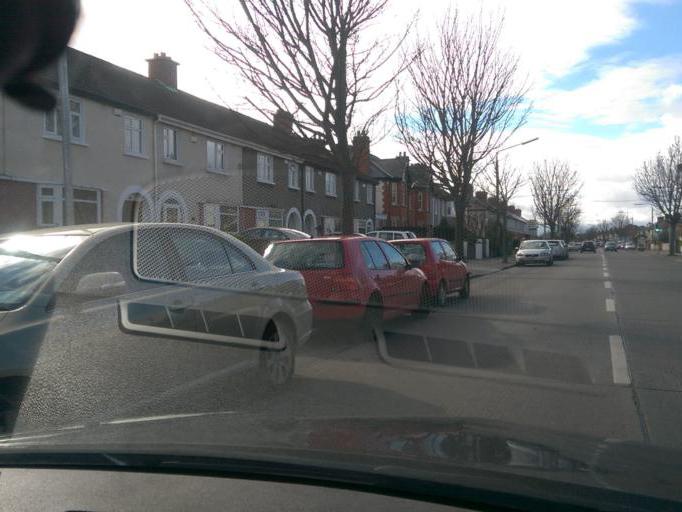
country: IE
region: Leinster
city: Artane
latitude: 53.3770
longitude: -6.2237
